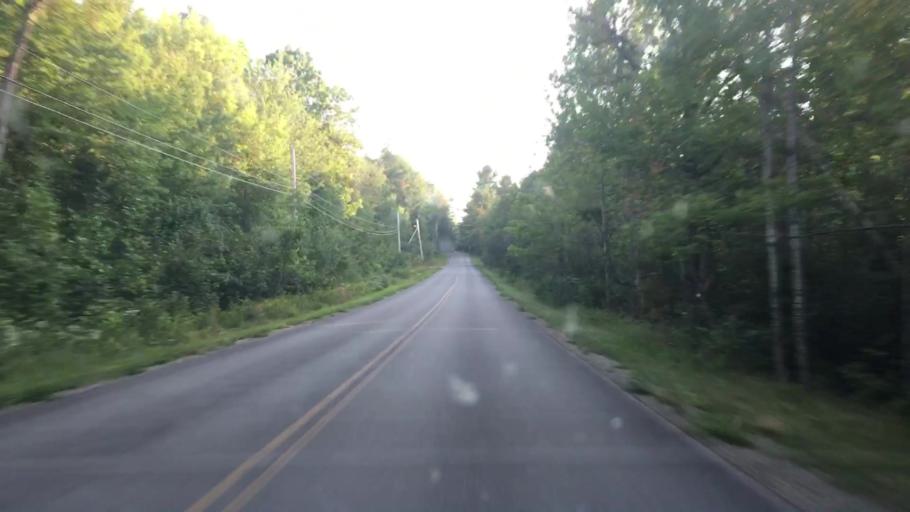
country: US
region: Maine
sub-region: Penobscot County
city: Hampden
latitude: 44.7037
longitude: -68.8906
